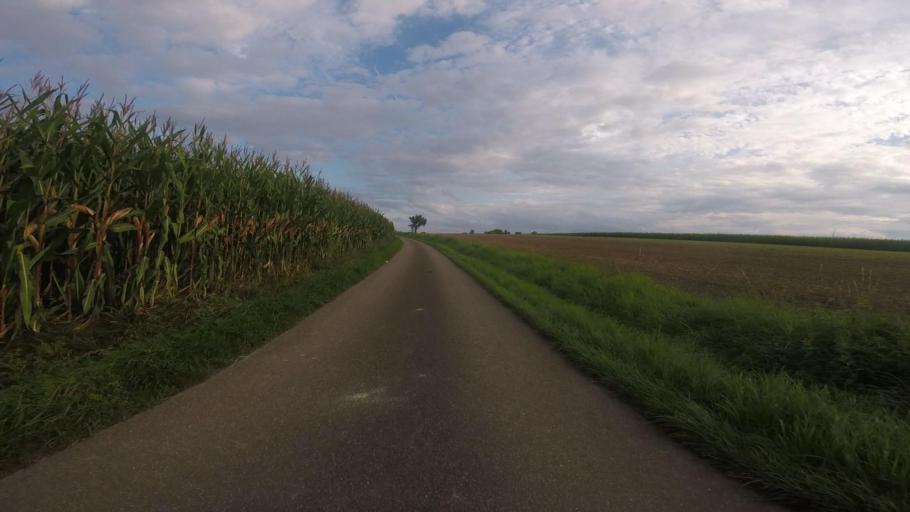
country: DE
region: Baden-Wuerttemberg
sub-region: Regierungsbezirk Stuttgart
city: Oberstenfeld
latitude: 49.0134
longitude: 9.3595
